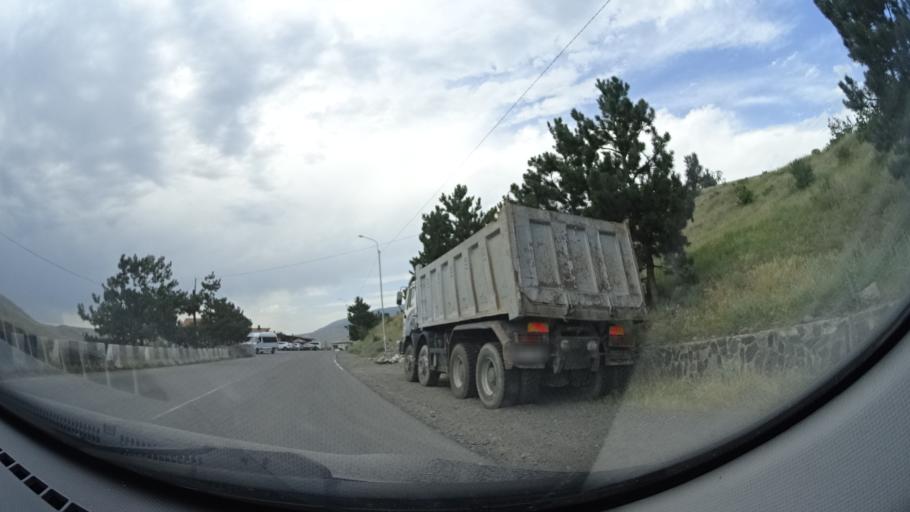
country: GE
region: Samtskhe-Javakheti
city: Aspindza
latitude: 41.5776
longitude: 43.2438
